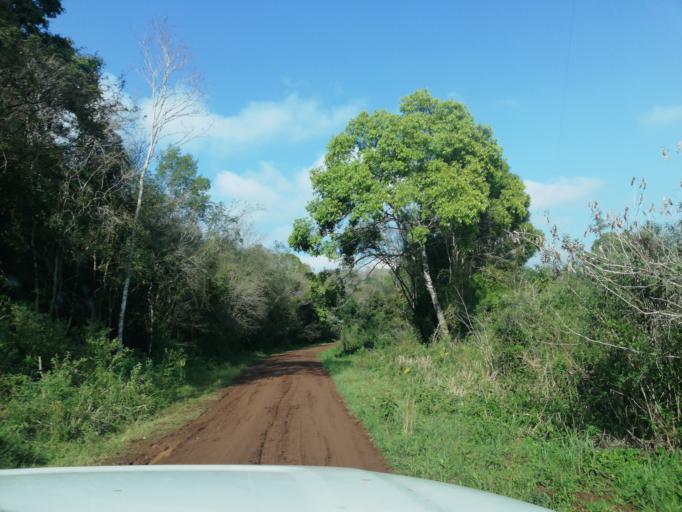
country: AR
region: Misiones
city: Cerro Azul
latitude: -27.5971
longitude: -55.5238
